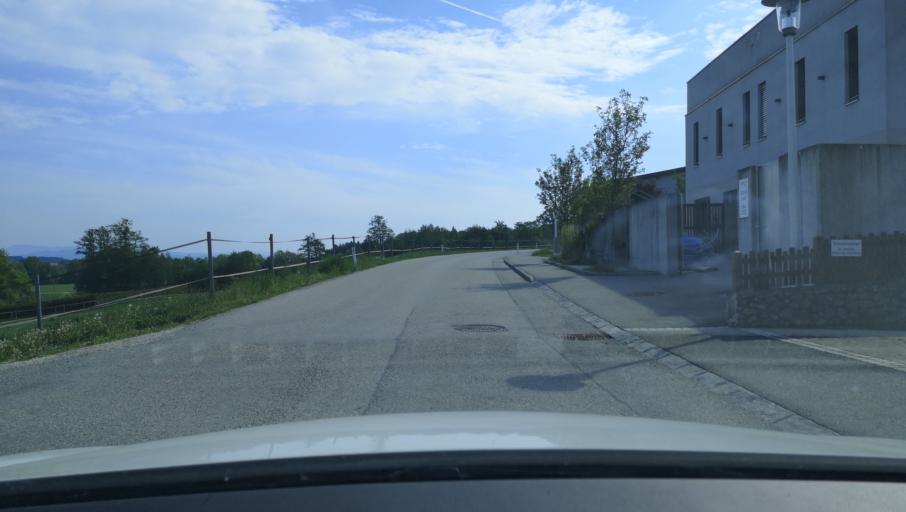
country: AT
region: Lower Austria
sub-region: Politischer Bezirk Amstetten
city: Neuhofen an der Ybbs
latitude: 48.0583
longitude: 14.8636
